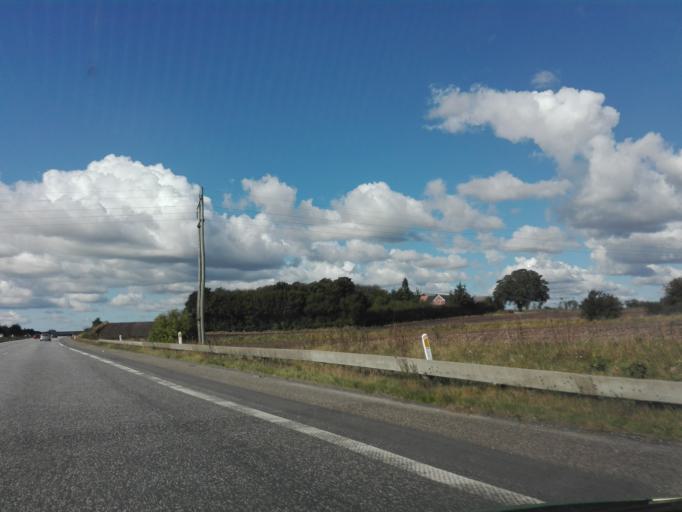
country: DK
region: North Denmark
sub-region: Mariagerfjord Kommune
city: Mariager
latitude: 56.5447
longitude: 9.8918
